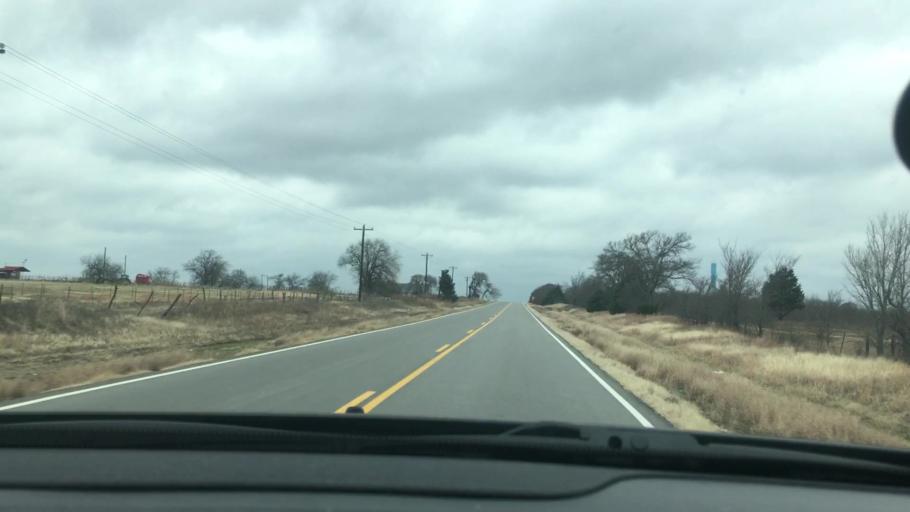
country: US
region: Oklahoma
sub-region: Atoka County
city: Atoka
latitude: 34.3749
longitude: -96.2445
